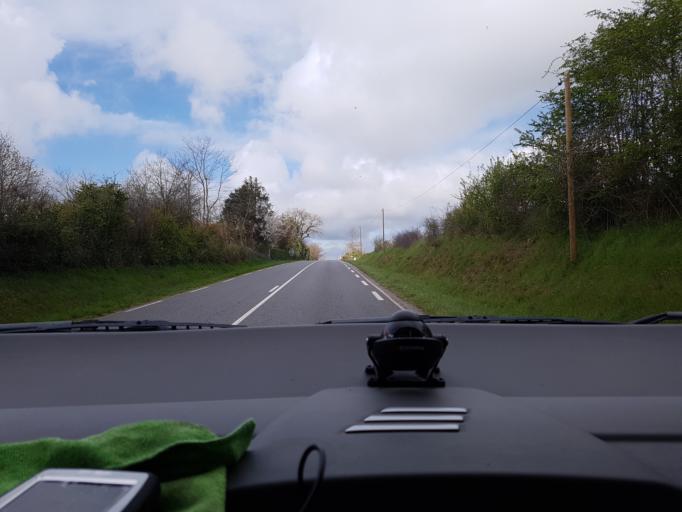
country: FR
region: Midi-Pyrenees
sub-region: Departement de l'Aveyron
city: Colombies
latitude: 44.4013
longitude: 2.3412
